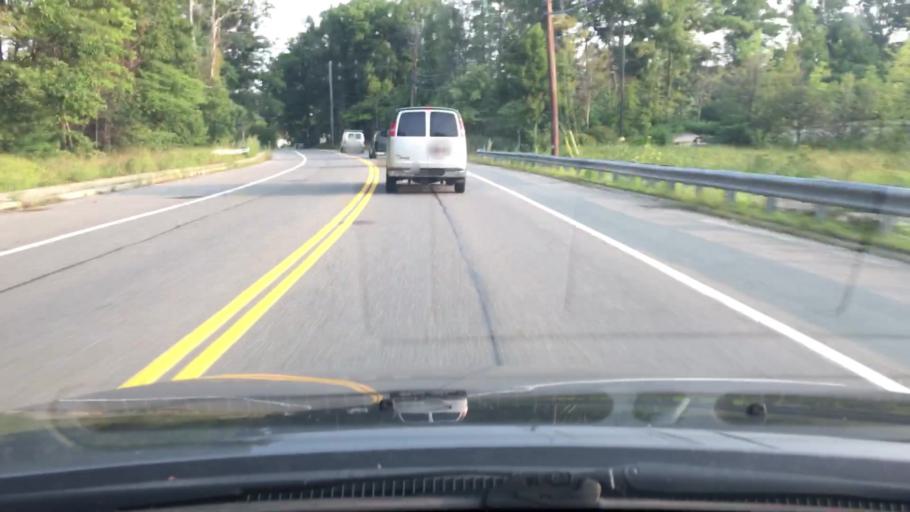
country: US
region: Massachusetts
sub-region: Middlesex County
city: Hopkinton
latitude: 42.1974
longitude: -71.5409
